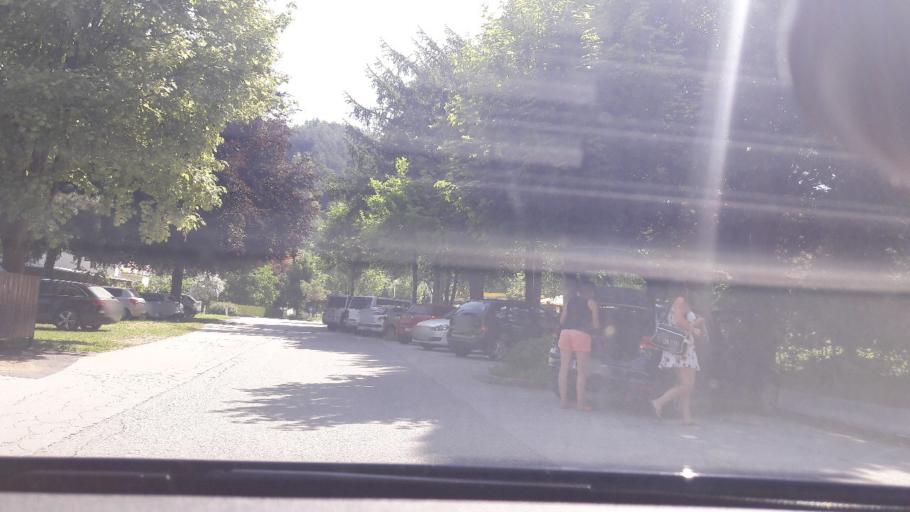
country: AT
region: Styria
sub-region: Politischer Bezirk Voitsberg
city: Kohlschwarz
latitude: 47.0834
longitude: 15.1244
